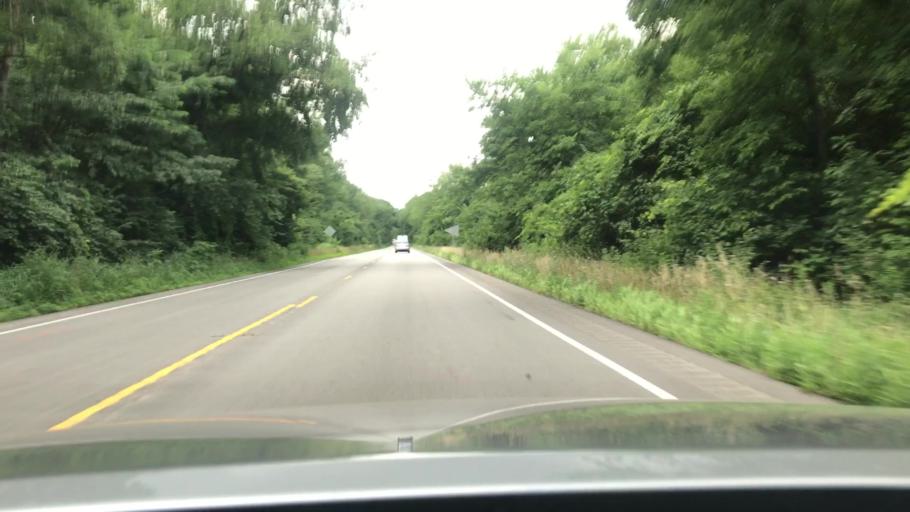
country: US
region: Illinois
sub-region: DuPage County
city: Burr Ridge
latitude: 41.7160
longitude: -87.9012
